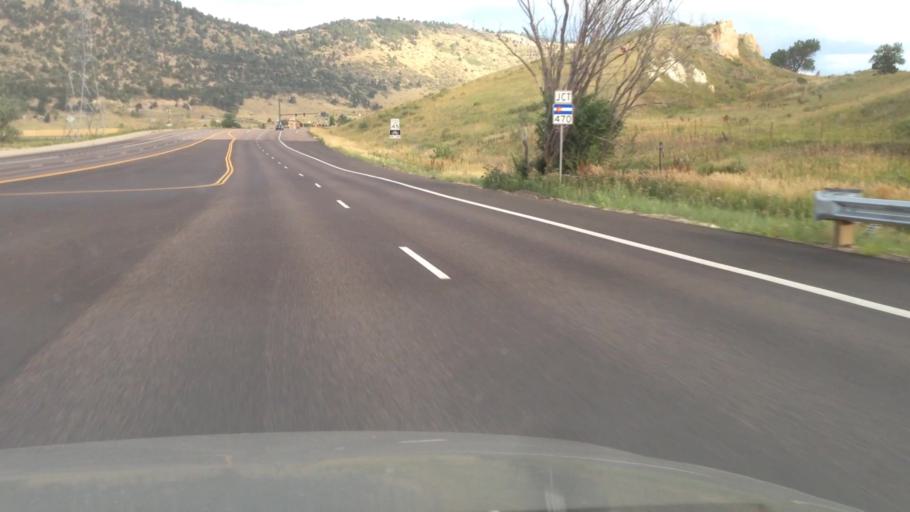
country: US
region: Colorado
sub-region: Jefferson County
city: West Pleasant View
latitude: 39.6846
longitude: -105.1826
